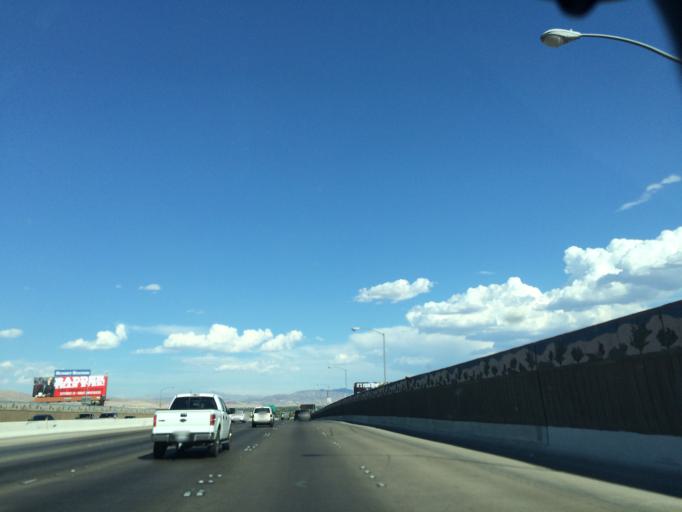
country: US
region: Nevada
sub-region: Clark County
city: Las Vegas
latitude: 36.1706
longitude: -115.1313
